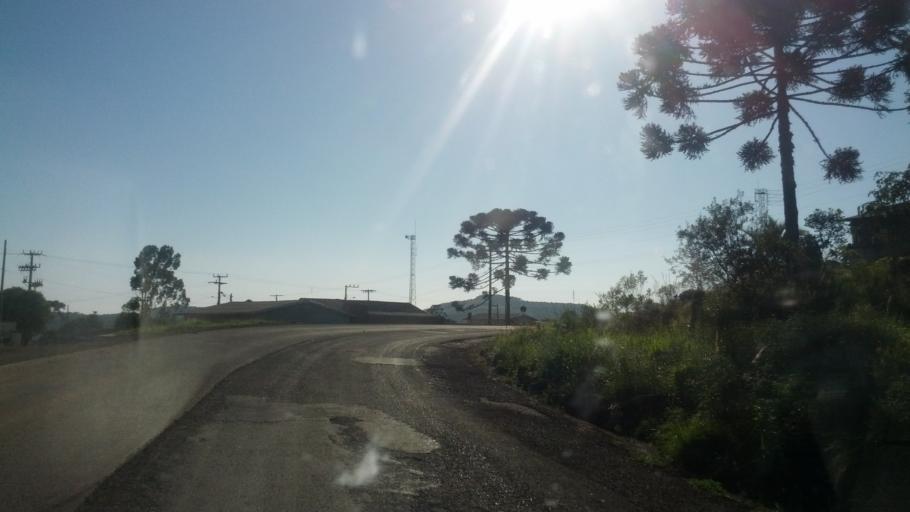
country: BR
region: Santa Catarina
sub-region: Lages
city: Lages
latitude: -27.9368
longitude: -50.5148
